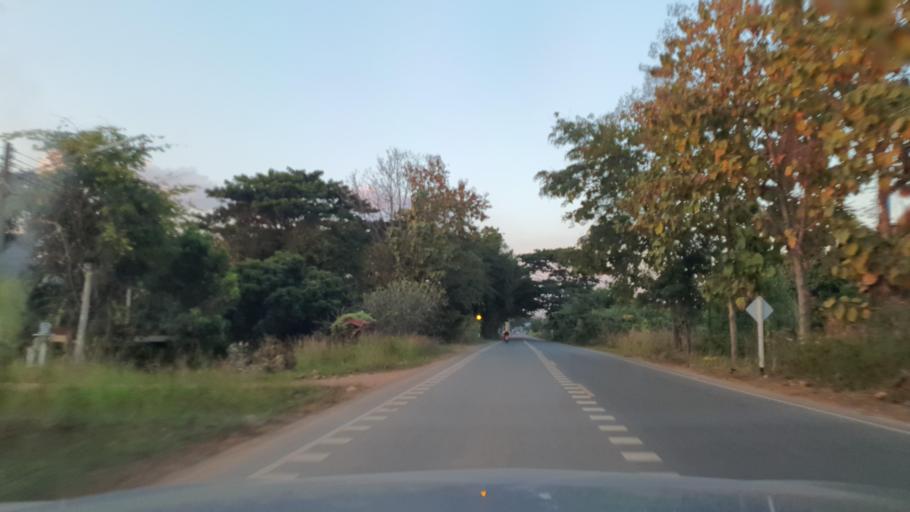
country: TH
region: Phayao
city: Dok Kham Tai
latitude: 19.0212
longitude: 100.0624
